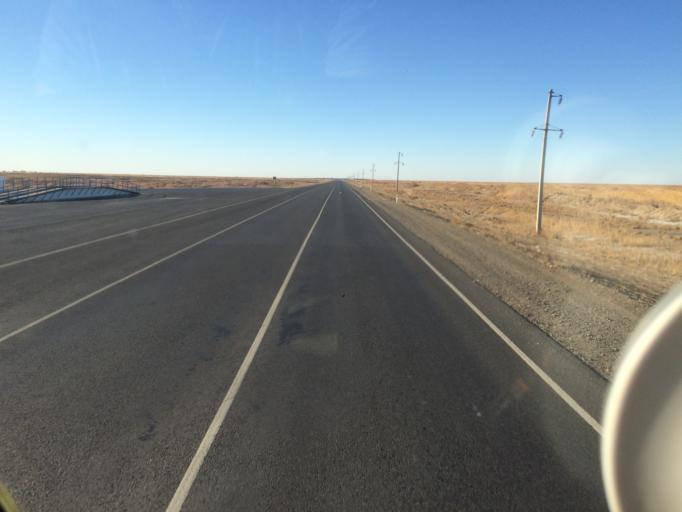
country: KZ
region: Qyzylorda
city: Zhosaly
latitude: 45.0981
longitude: 64.2433
